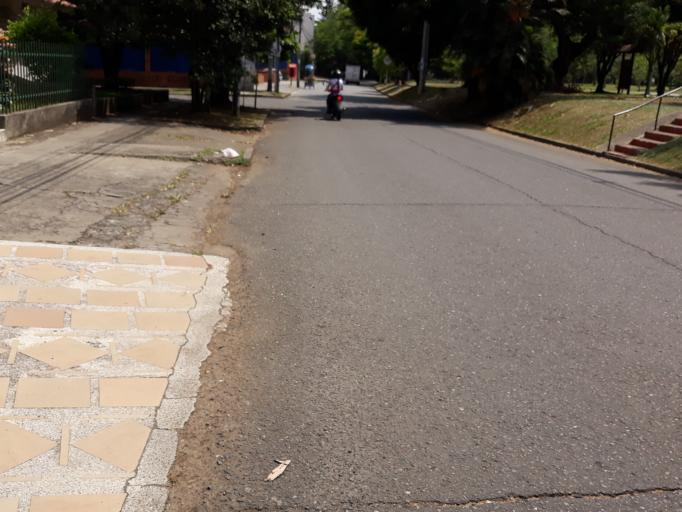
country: CO
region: Valle del Cauca
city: Cali
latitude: 3.3804
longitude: -76.5410
